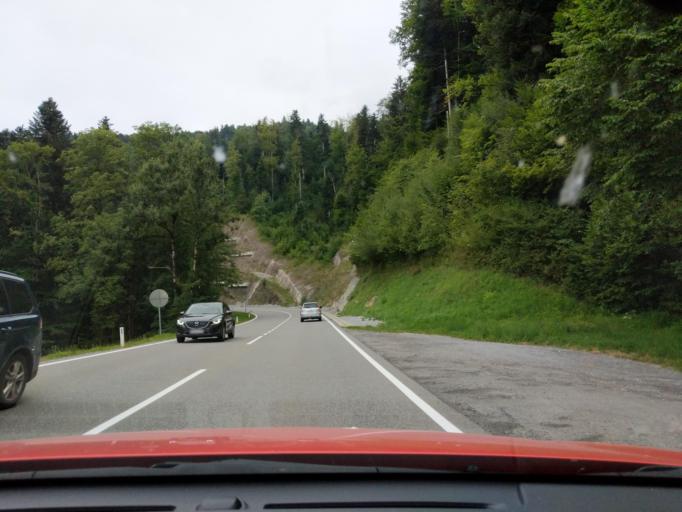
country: AT
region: Vorarlberg
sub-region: Politischer Bezirk Bregenz
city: Egg
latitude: 47.4487
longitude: 9.8822
